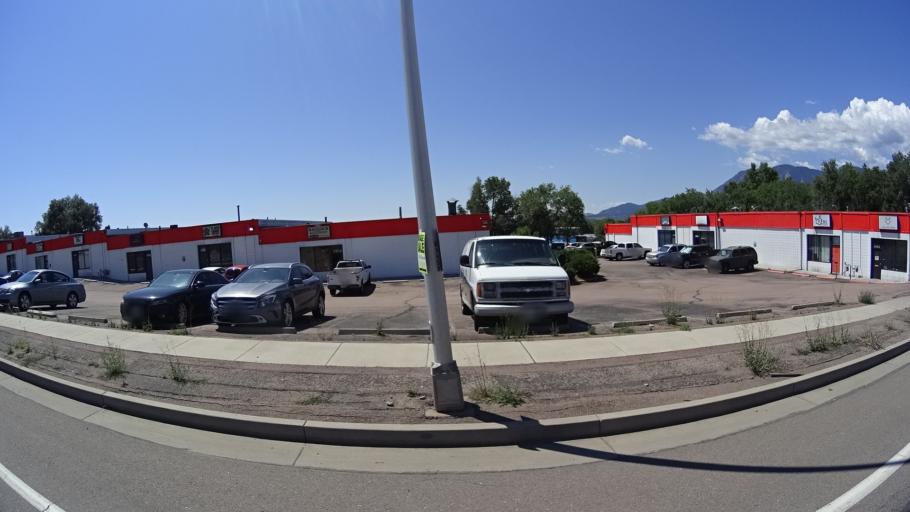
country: US
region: Colorado
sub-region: El Paso County
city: Stratmoor
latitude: 38.7963
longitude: -104.7743
